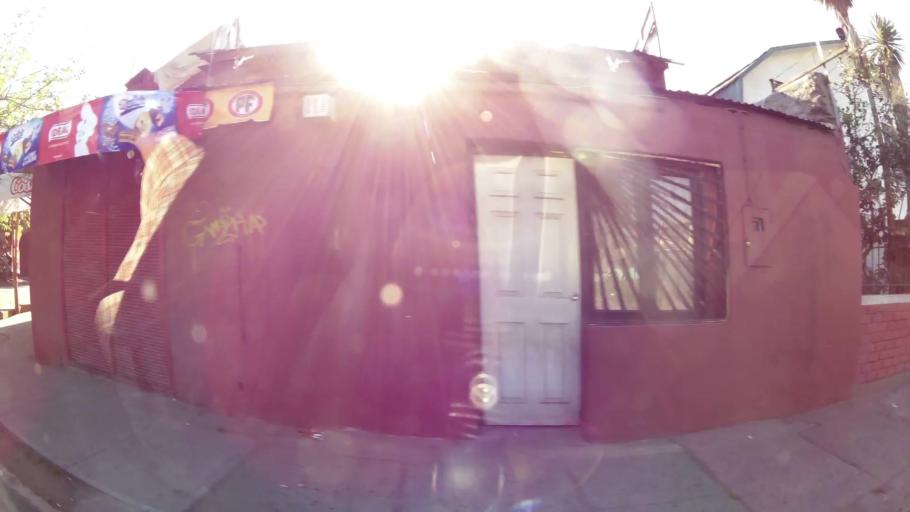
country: CL
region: Santiago Metropolitan
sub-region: Provincia de Santiago
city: Santiago
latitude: -33.3878
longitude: -70.6710
